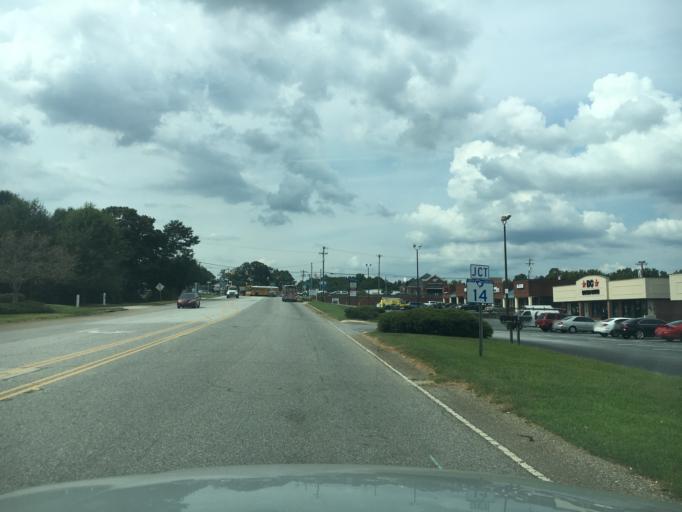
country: US
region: South Carolina
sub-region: Greenville County
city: Five Forks
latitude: 34.8502
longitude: -82.2289
